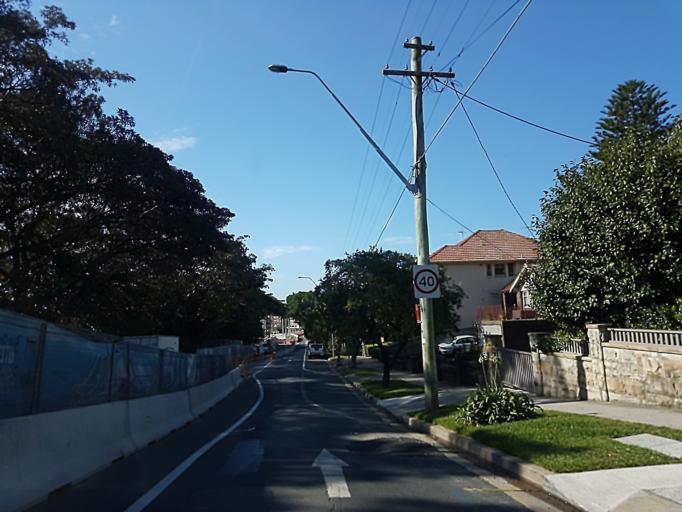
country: AU
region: New South Wales
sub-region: Randwick
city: Kingsford
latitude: -33.9142
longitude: 151.2352
